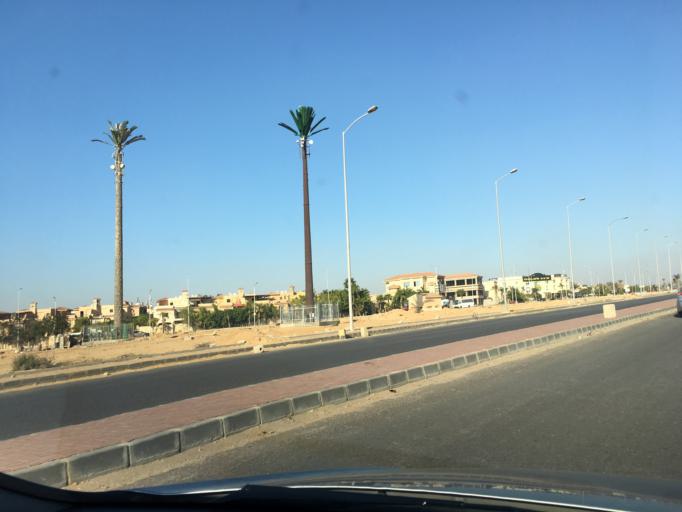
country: EG
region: Al Jizah
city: Madinat Sittah Uktubar
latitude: 29.9988
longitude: 30.9572
